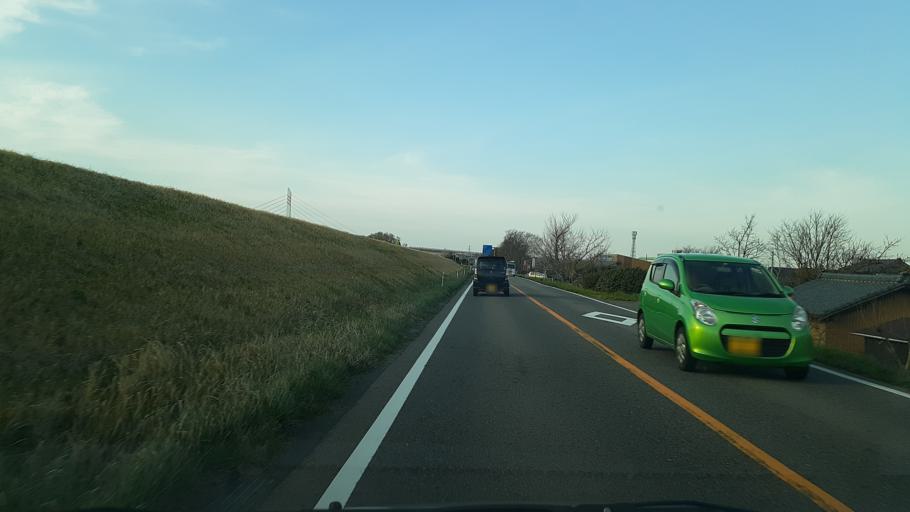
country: JP
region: Niigata
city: Niigata-shi
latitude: 37.8642
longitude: 139.0256
